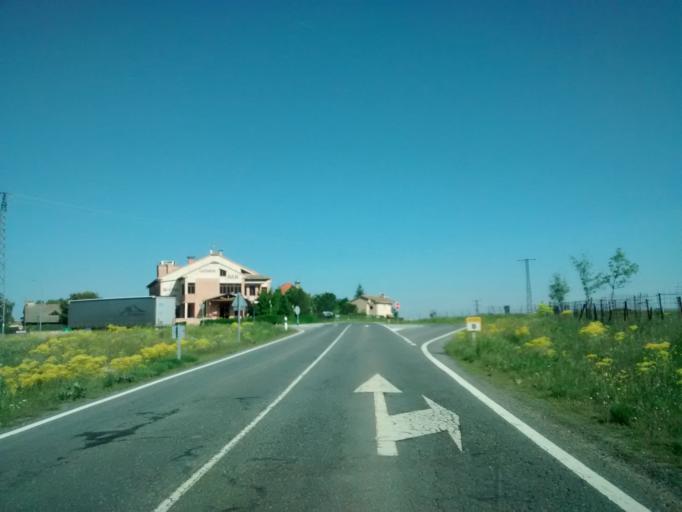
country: ES
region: Castille and Leon
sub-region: Provincia de Segovia
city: Trescasas
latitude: 40.9637
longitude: -4.0328
